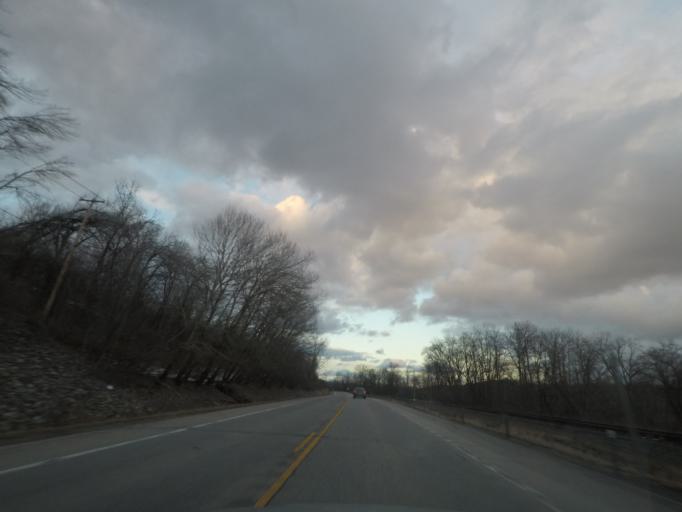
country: US
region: New York
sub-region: Montgomery County
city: Fonda
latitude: 42.9309
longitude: -74.4247
